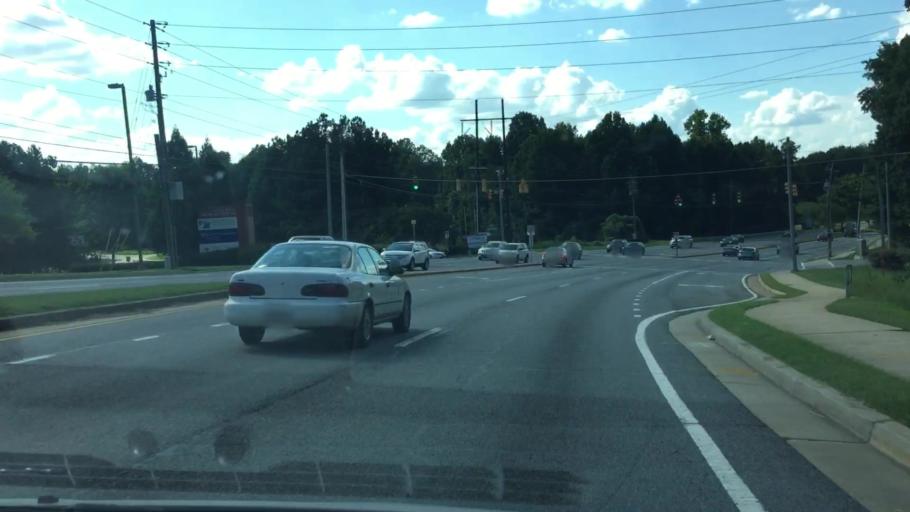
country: US
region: Georgia
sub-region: Cobb County
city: Austell
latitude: 33.8545
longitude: -84.6133
